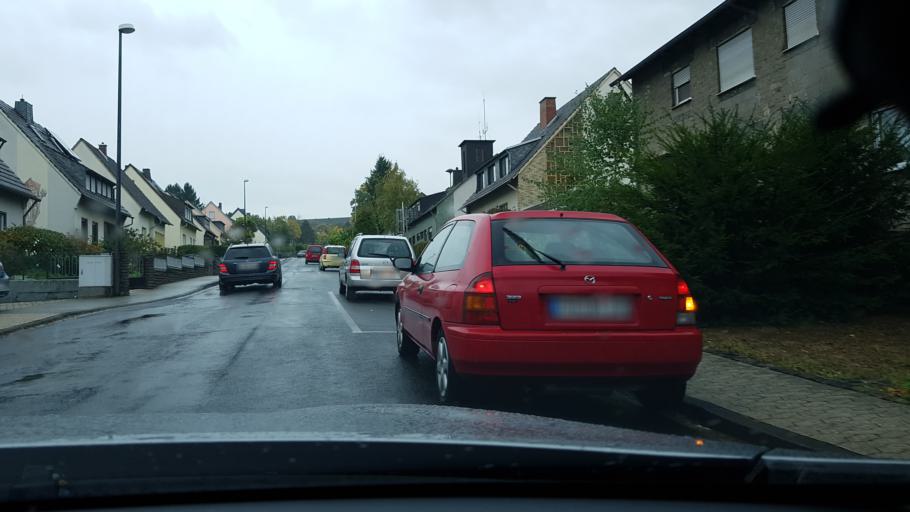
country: DE
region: Rheinland-Pfalz
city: Urbar
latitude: 50.3805
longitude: 7.6258
